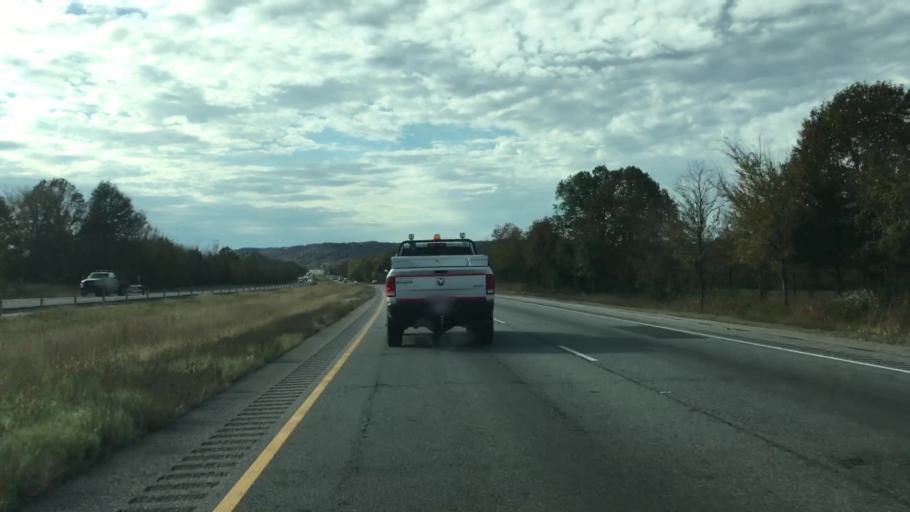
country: US
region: Arkansas
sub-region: Pope County
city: Atkins
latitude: 35.2515
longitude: -92.8930
